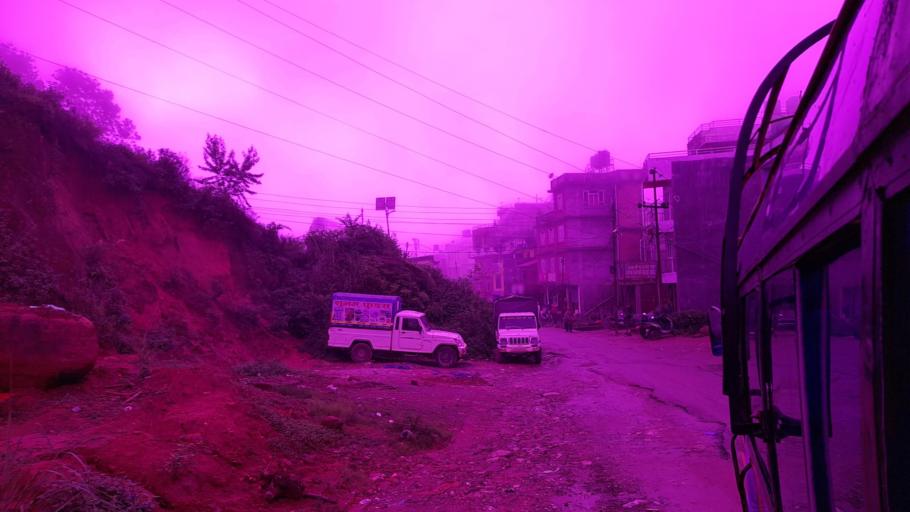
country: NP
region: Central Region
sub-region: Bagmati Zone
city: Kathmandu
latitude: 27.8322
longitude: 85.2410
